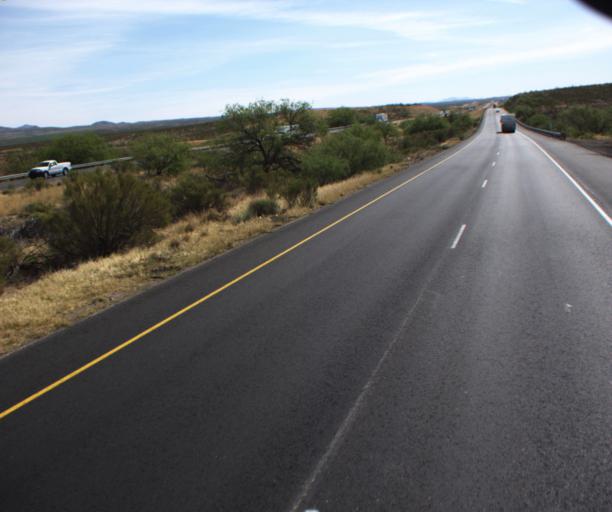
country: US
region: Arizona
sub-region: Pima County
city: Vail
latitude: 31.9879
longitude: -110.5883
